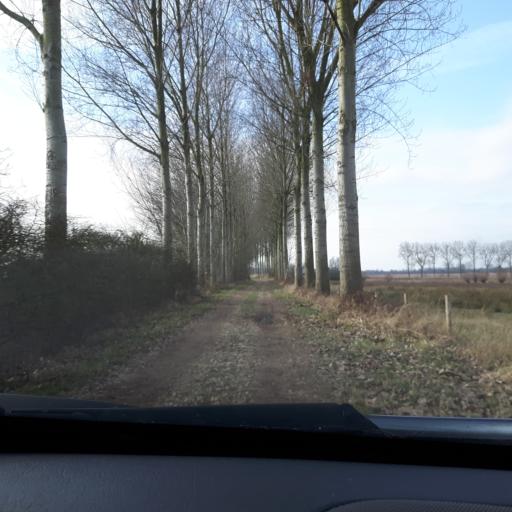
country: NL
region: Zeeland
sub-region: Gemeente Goes
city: Goes
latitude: 51.4467
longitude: 3.8987
